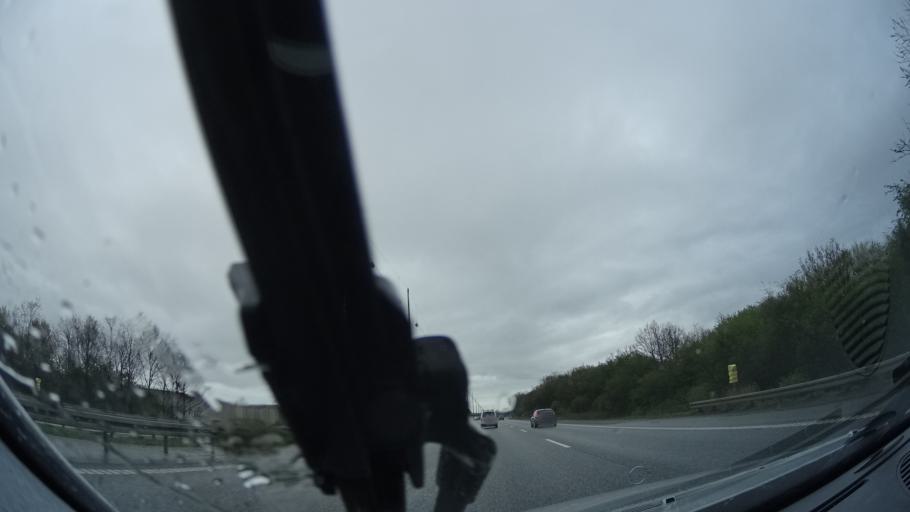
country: DK
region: Capital Region
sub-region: Brondby Kommune
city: Brondbyvester
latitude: 55.6421
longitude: 12.3914
